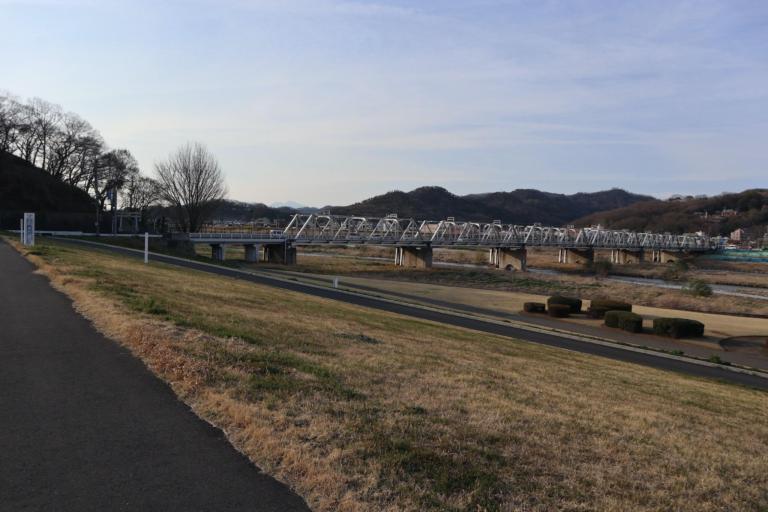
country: JP
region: Tochigi
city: Ashikaga
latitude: 36.3319
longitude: 139.4445
